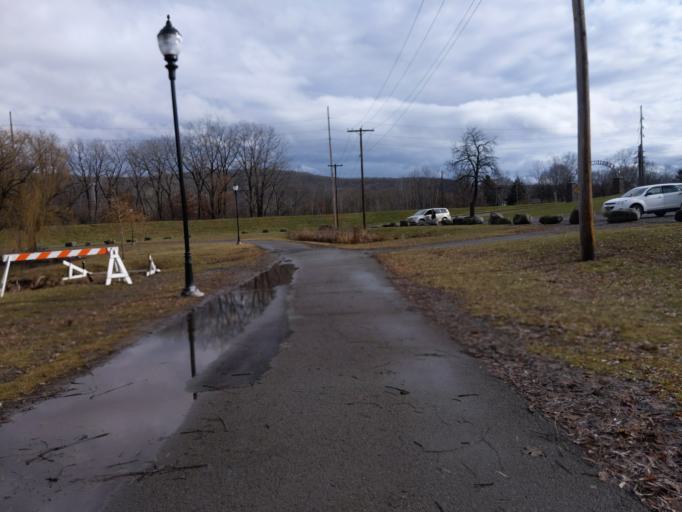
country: US
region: New York
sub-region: Chemung County
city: Elmira Heights
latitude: 42.1128
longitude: -76.8162
